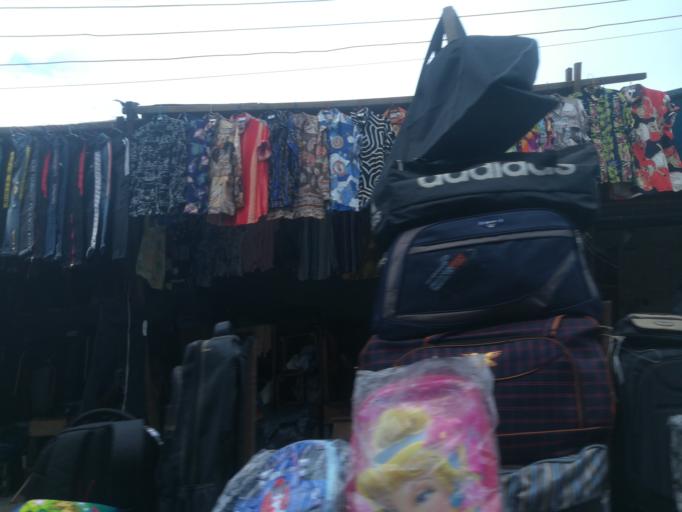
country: NG
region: Lagos
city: Lagos
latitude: 6.4560
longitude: 3.3869
